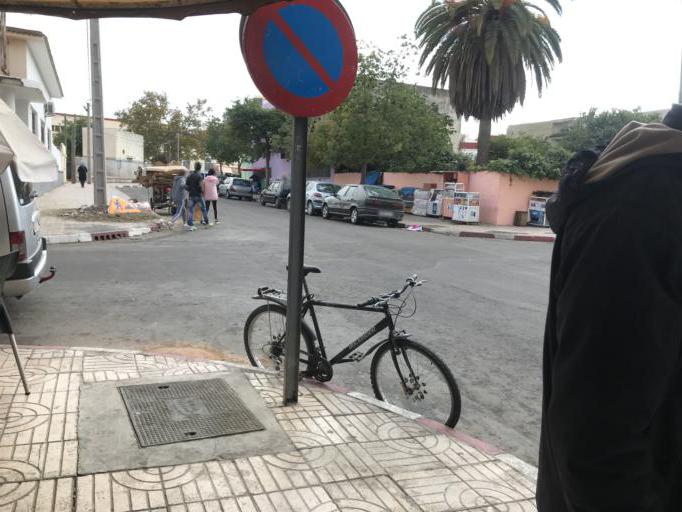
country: MA
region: Taza-Al Hoceima-Taounate
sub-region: Taza
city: Taza
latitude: 34.2231
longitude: -4.0074
